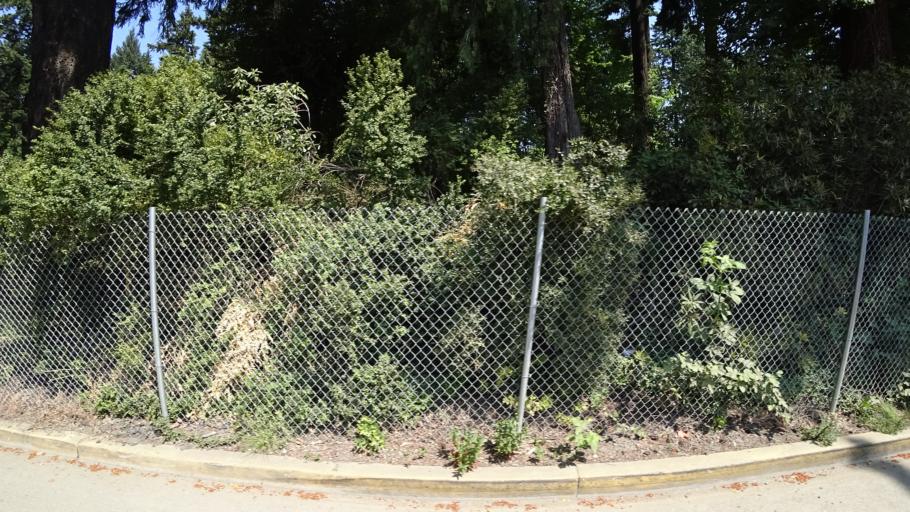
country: US
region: Oregon
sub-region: Multnomah County
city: Portland
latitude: 45.5210
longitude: -122.7027
